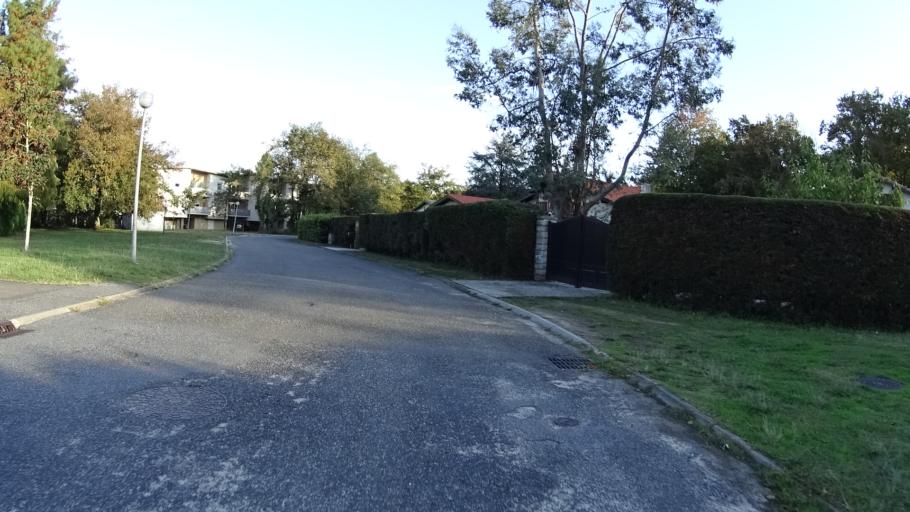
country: FR
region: Aquitaine
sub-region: Departement des Landes
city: Saint-Paul-les-Dax
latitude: 43.7381
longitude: -1.0478
